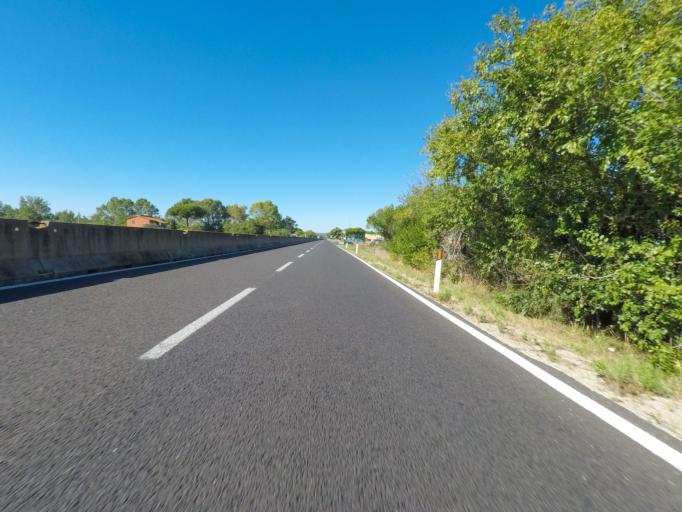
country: IT
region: Tuscany
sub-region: Provincia di Grosseto
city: Albinia
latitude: 42.4844
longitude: 11.2184
